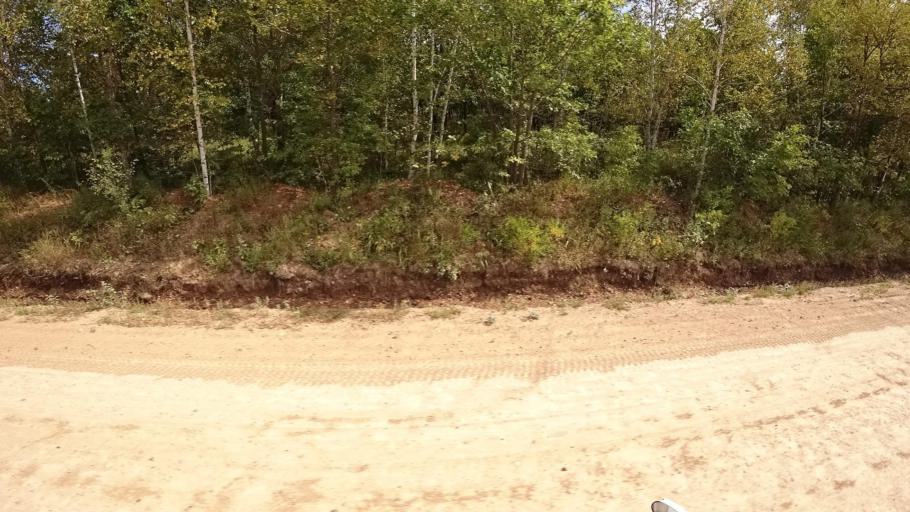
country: RU
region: Primorskiy
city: Yakovlevka
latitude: 44.7320
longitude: 133.6090
